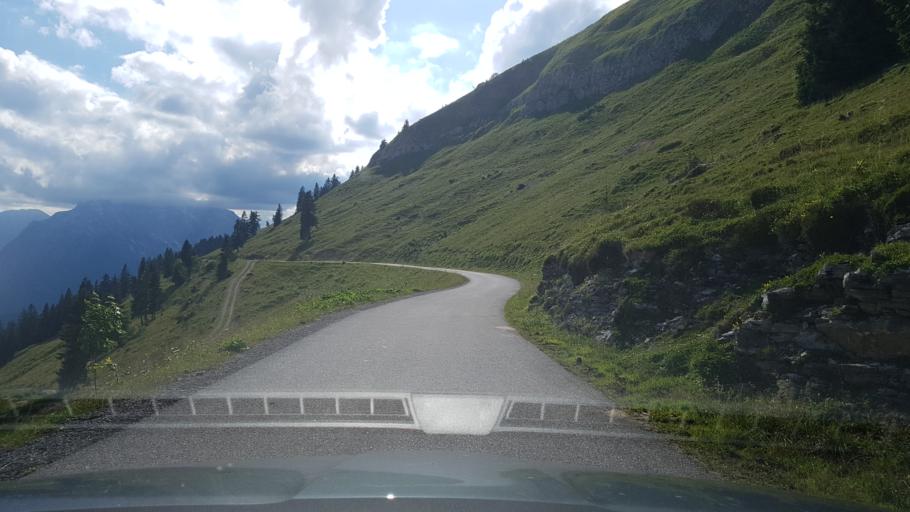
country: AT
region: Salzburg
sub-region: Politischer Bezirk Salzburg-Umgebung
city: Hintersee
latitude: 47.6370
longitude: 13.2738
